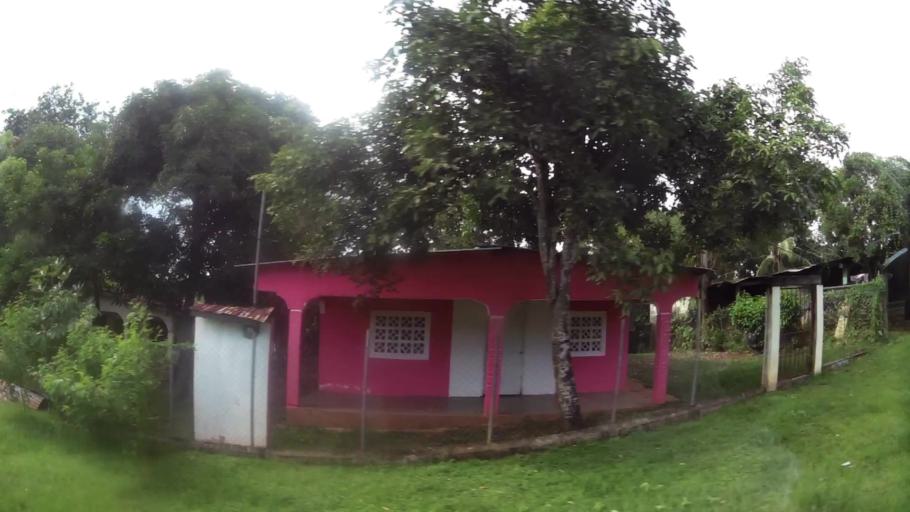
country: PA
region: Panama
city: El Coco
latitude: 8.8724
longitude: -79.8044
